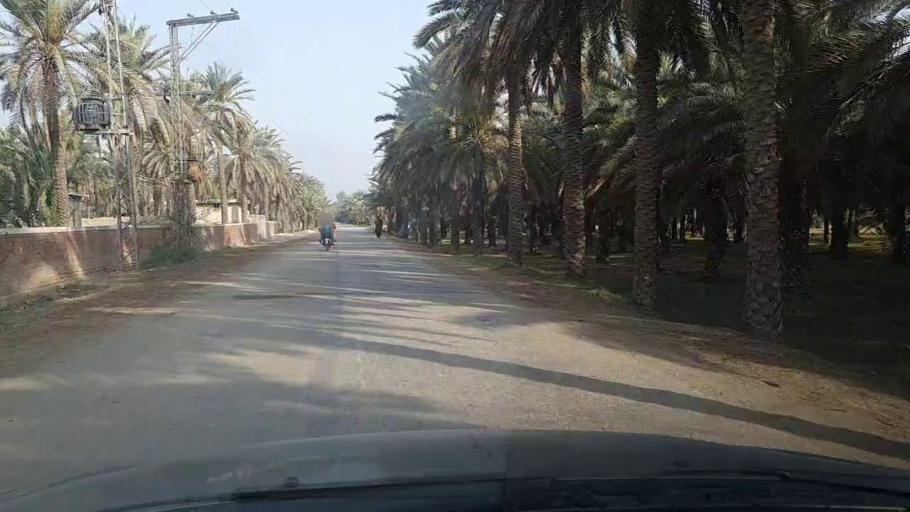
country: PK
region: Sindh
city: Pir jo Goth
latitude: 27.5586
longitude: 68.5553
